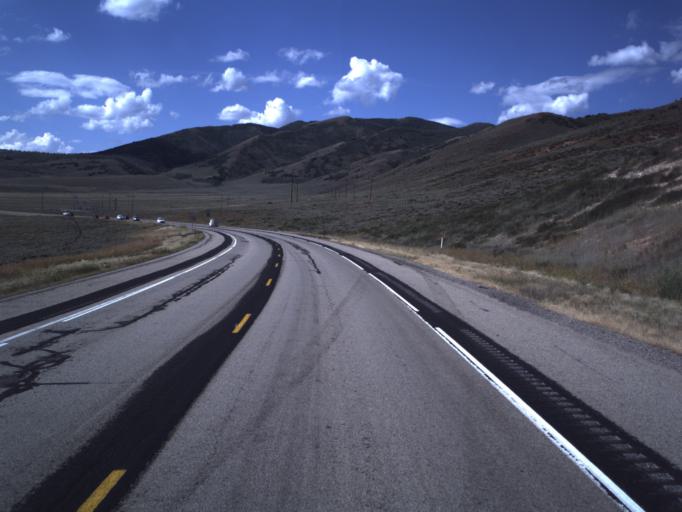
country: US
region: Utah
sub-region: Wasatch County
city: Heber
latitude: 40.2205
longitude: -111.1044
